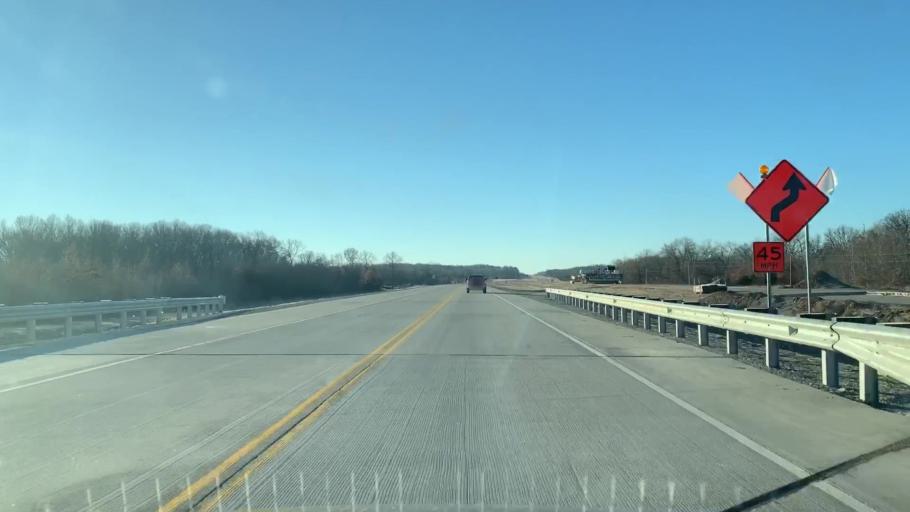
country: US
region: Kansas
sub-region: Crawford County
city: Arma
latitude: 37.6805
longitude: -94.7033
